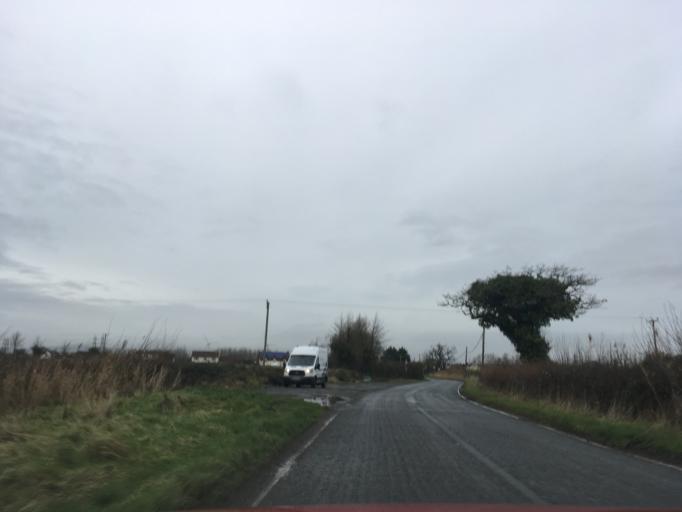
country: GB
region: Wales
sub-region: Newport
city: Nash
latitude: 51.5489
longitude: -2.9397
